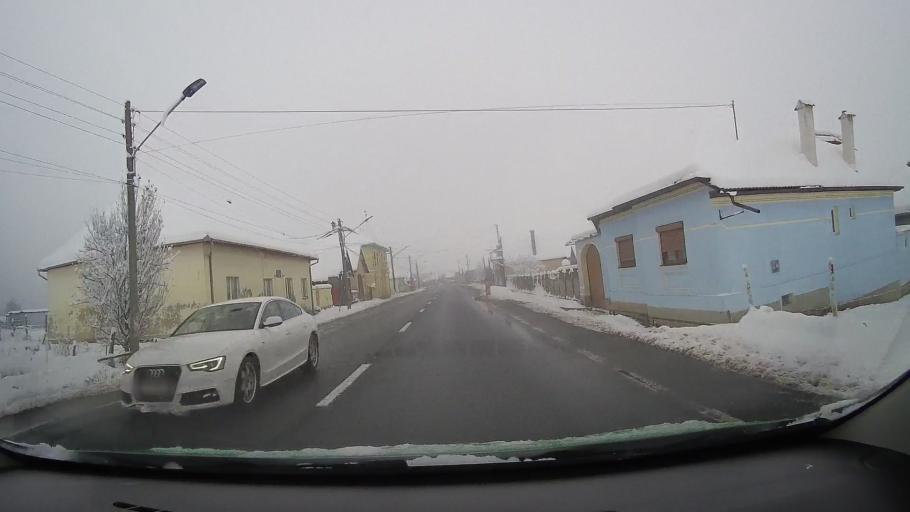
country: RO
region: Sibiu
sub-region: Comuna Orlat
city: Orlat
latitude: 45.7851
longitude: 23.9359
